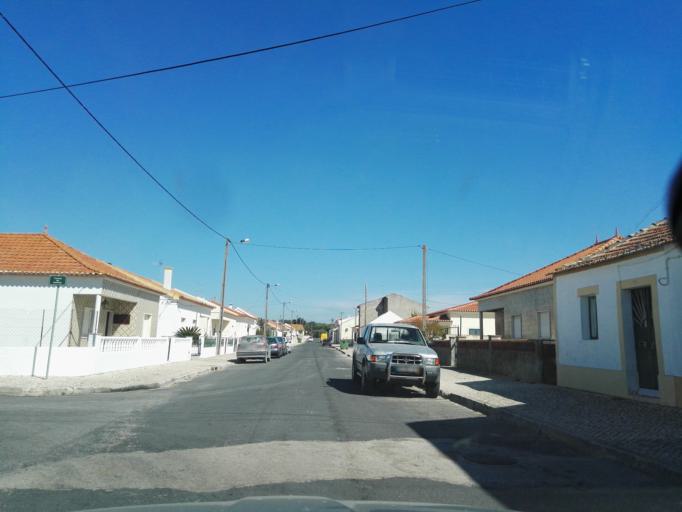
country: PT
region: Santarem
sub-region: Benavente
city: Poceirao
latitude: 38.8638
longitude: -8.7450
